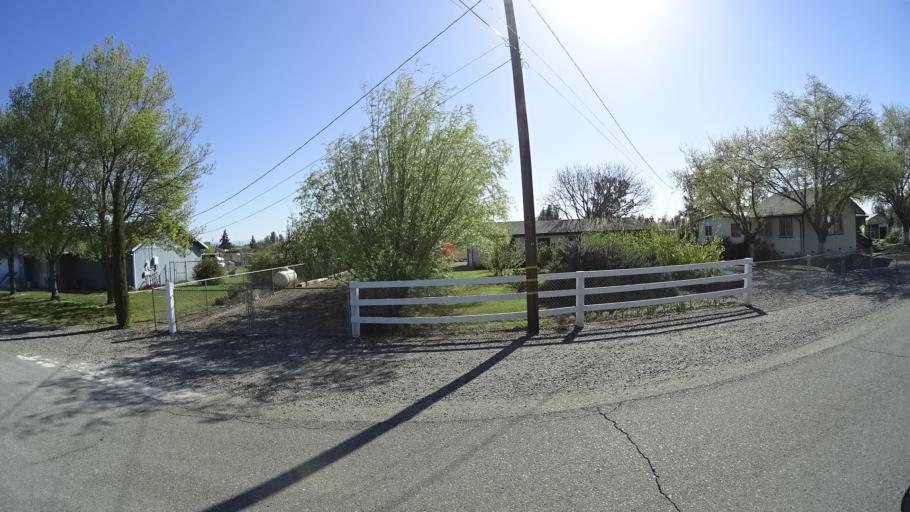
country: US
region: California
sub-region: Glenn County
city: Orland
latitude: 39.7457
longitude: -122.2083
